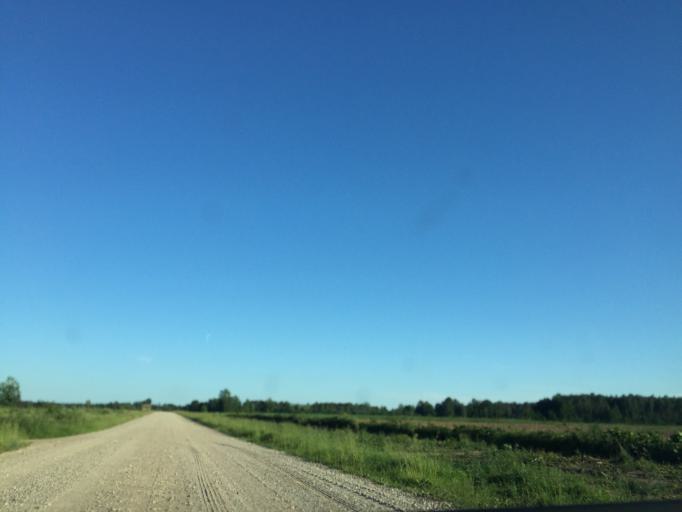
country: LV
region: Broceni
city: Broceni
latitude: 56.8476
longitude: 22.5646
